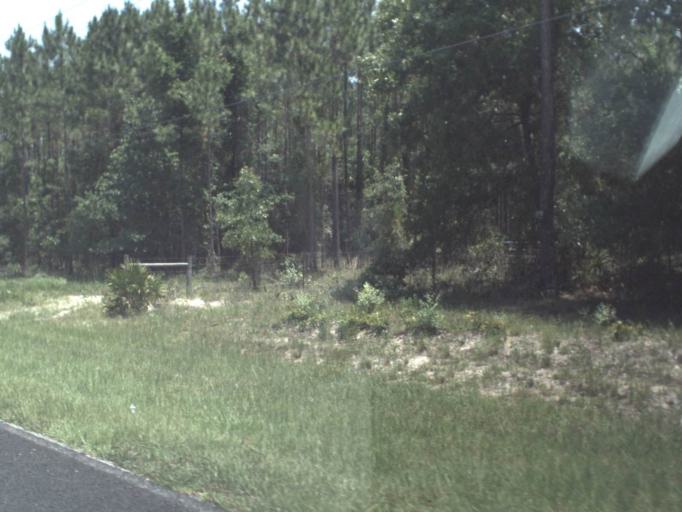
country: US
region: Florida
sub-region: Flagler County
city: Palm Coast
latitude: 29.6694
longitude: -81.2894
